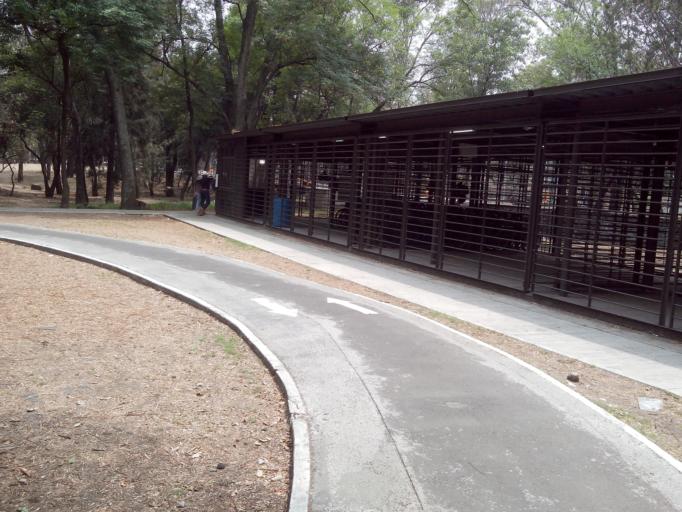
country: MX
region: Mexico City
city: Magdalena Contreras
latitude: 19.3258
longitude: -99.1879
